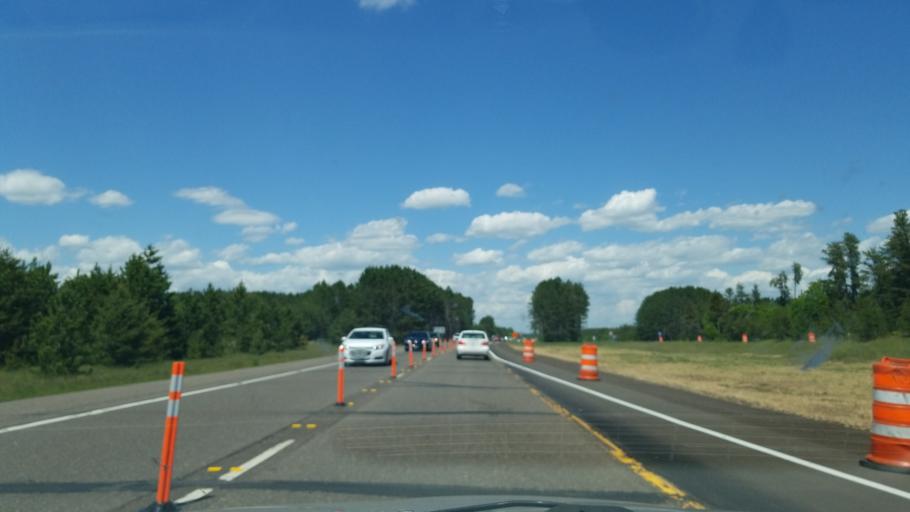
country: US
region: Minnesota
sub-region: Carlton County
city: Moose Lake
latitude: 46.3213
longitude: -92.8270
